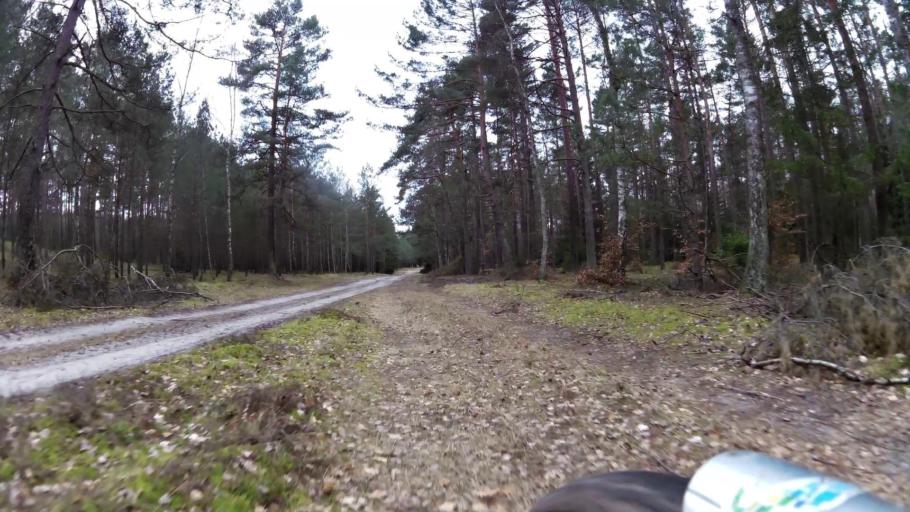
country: PL
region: Pomeranian Voivodeship
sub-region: Powiat bytowski
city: Trzebielino
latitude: 54.1243
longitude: 17.1318
